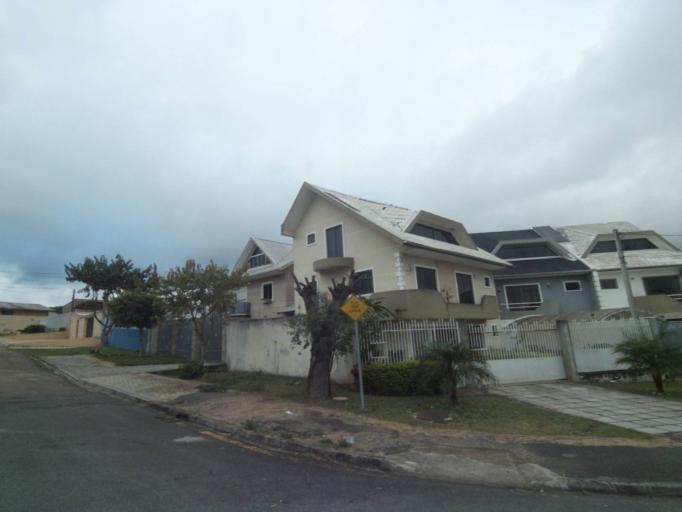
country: BR
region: Parana
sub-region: Curitiba
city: Curitiba
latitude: -25.5188
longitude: -49.3075
